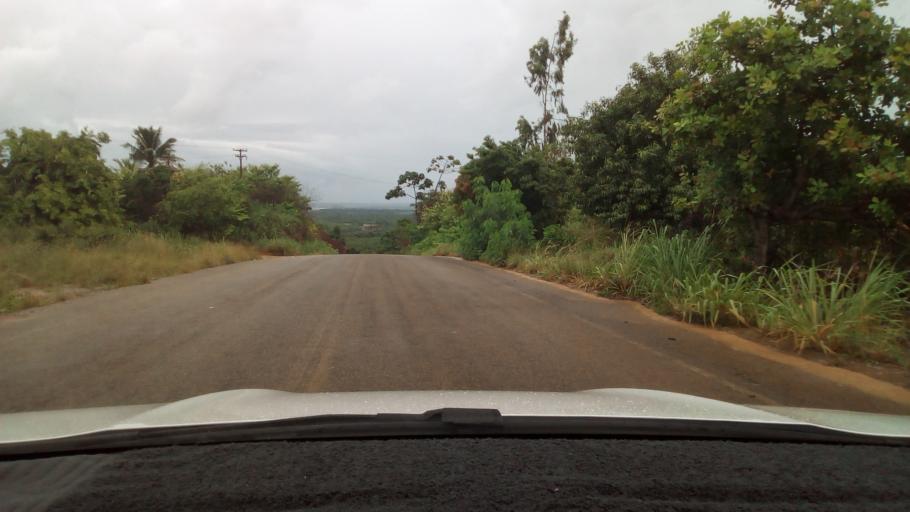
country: BR
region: Paraiba
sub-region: Pitimbu
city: Pitimbu
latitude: -7.4275
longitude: -34.8360
